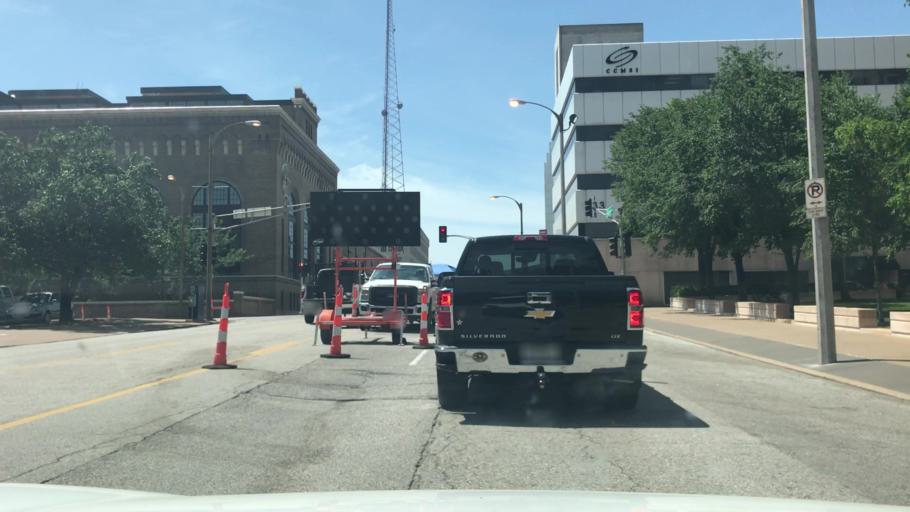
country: US
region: Missouri
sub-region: City of Saint Louis
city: St. Louis
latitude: 38.6248
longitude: -90.1972
